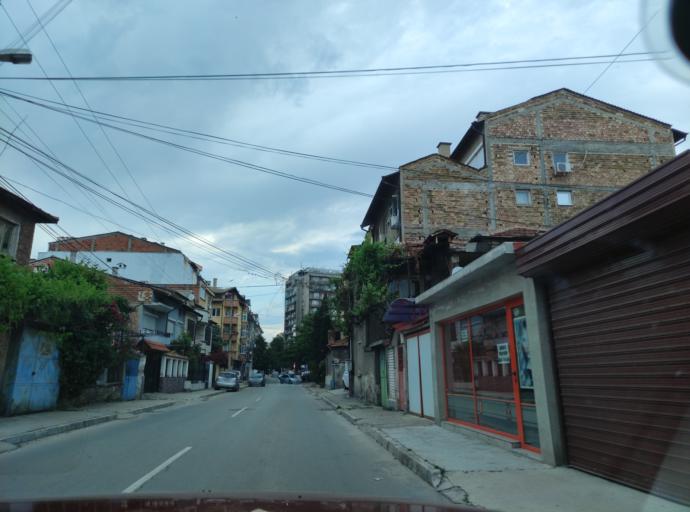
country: BG
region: Pazardzhik
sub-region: Obshtina Pazardzhik
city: Pazardzhik
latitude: 42.1849
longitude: 24.3348
